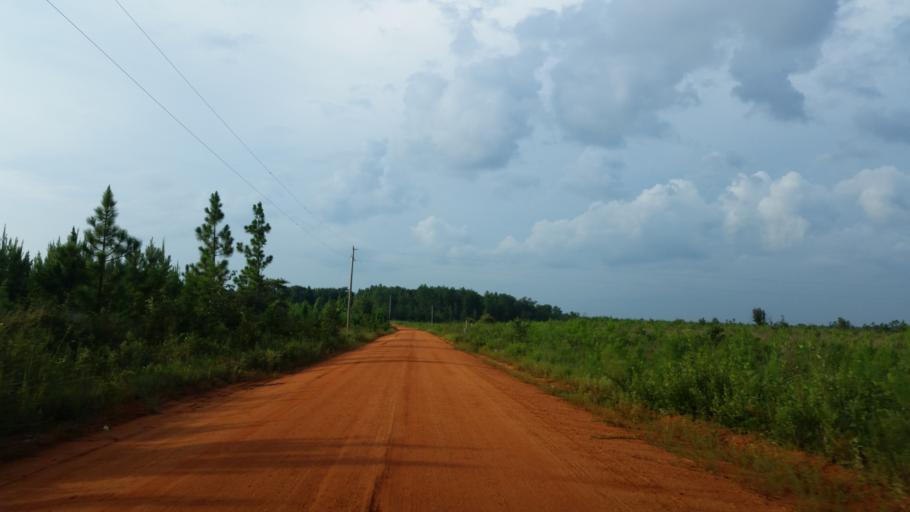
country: US
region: Alabama
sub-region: Escambia County
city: Atmore
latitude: 30.8598
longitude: -87.5786
